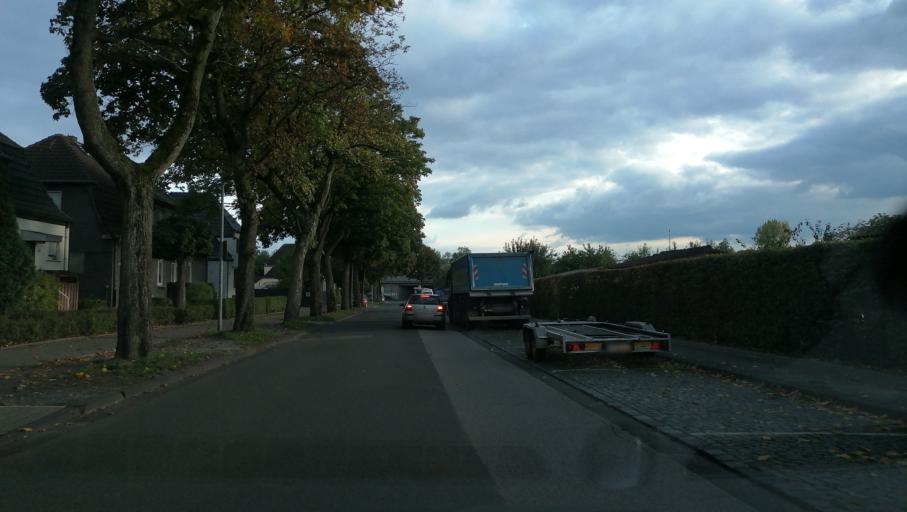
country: DE
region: North Rhine-Westphalia
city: Herten
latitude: 51.5719
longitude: 7.1124
